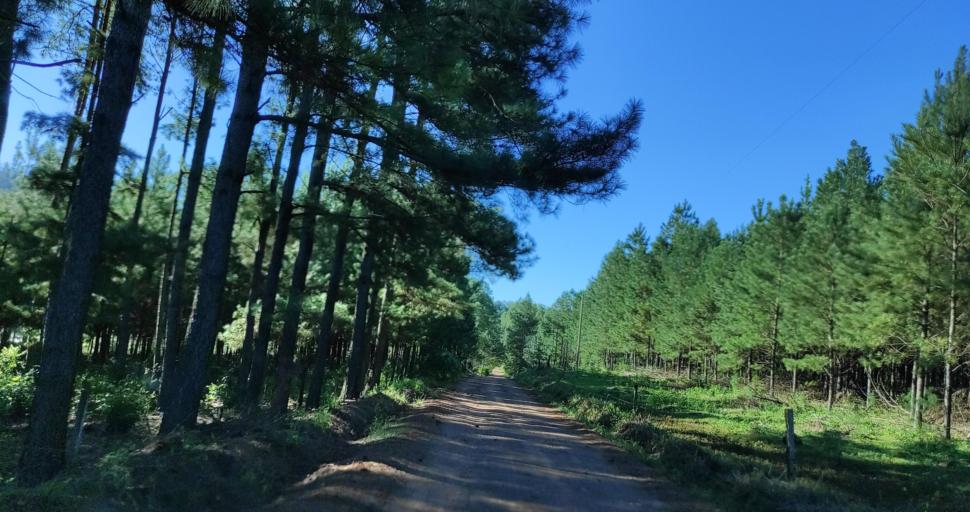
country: AR
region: Misiones
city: Capiovi
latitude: -26.9152
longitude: -54.9997
